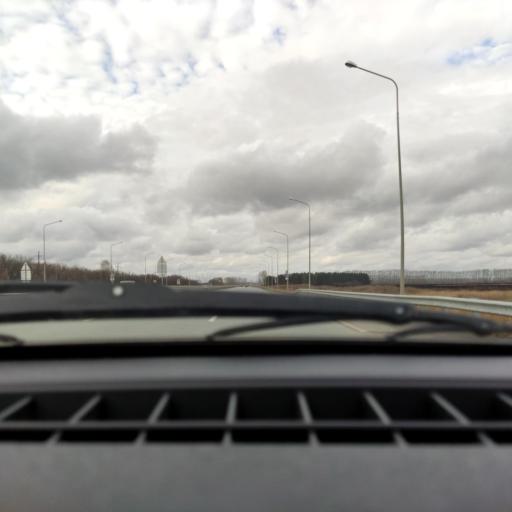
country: RU
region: Bashkortostan
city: Asanovo
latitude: 54.9148
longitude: 55.5914
